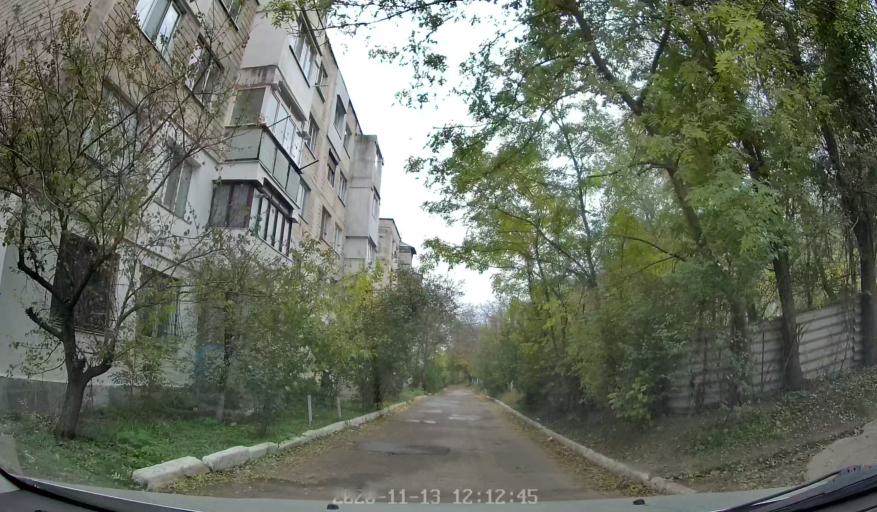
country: MD
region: Chisinau
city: Chisinau
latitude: 46.9548
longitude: 28.8367
